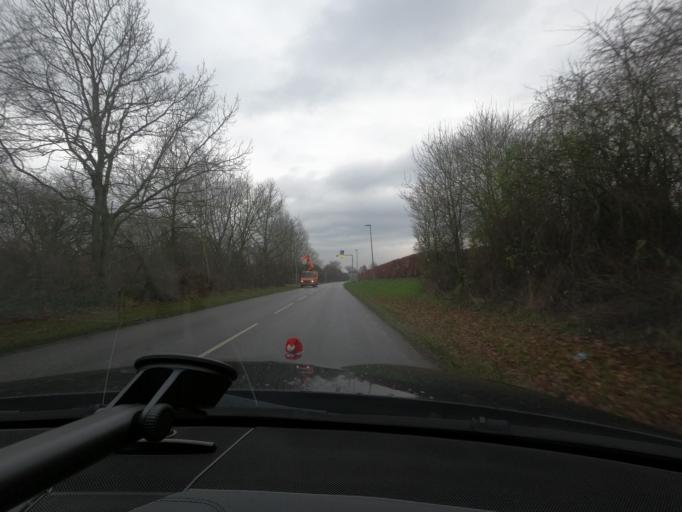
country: DK
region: South Denmark
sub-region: Sonderborg Kommune
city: Horuphav
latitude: 54.9177
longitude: 9.8963
